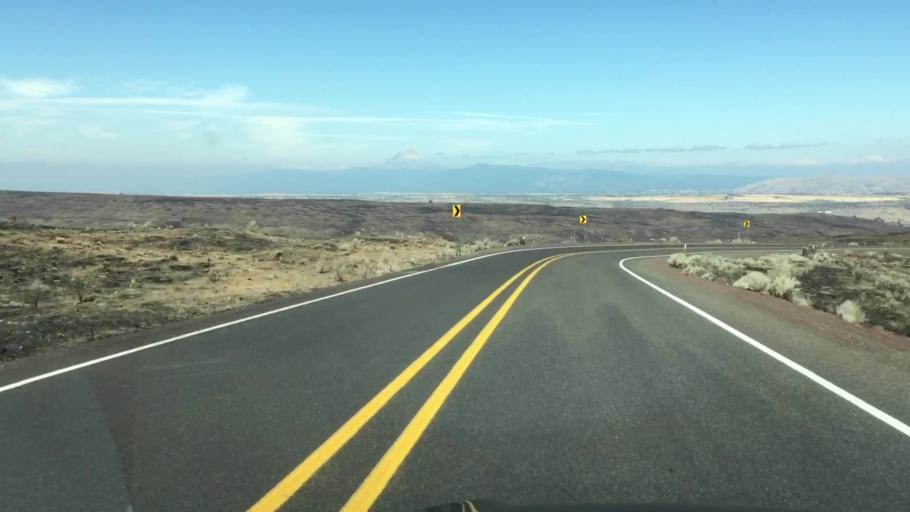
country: US
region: Oregon
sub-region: Jefferson County
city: Warm Springs
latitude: 45.1191
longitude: -121.0462
